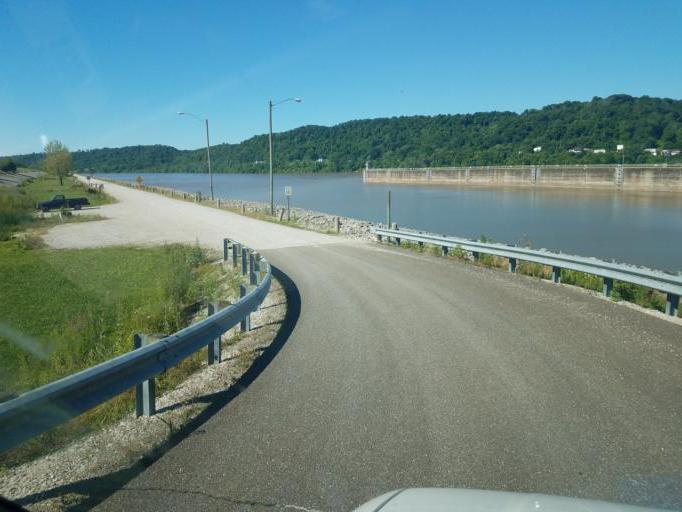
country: US
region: Ohio
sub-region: Gallia County
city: Gallipolis
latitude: 38.6802
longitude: -82.1828
